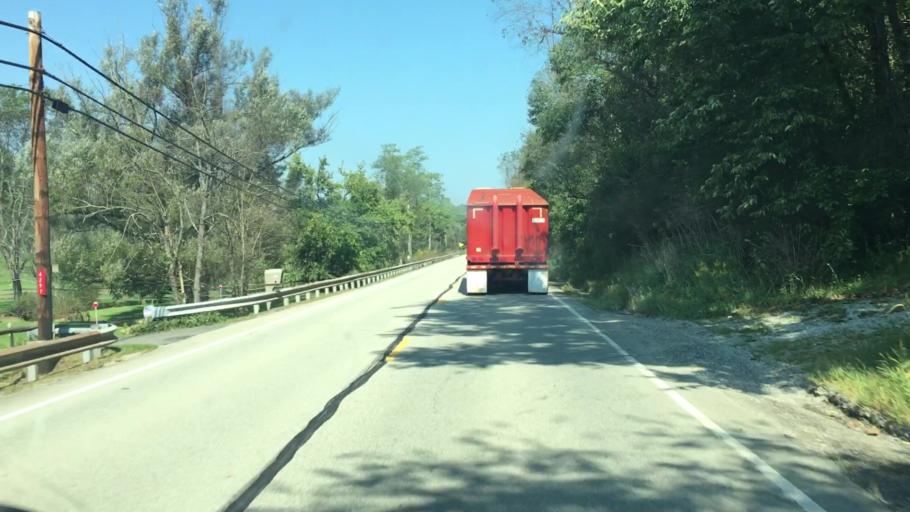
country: US
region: Pennsylvania
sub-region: Washington County
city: Washington
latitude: 40.0670
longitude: -80.2974
